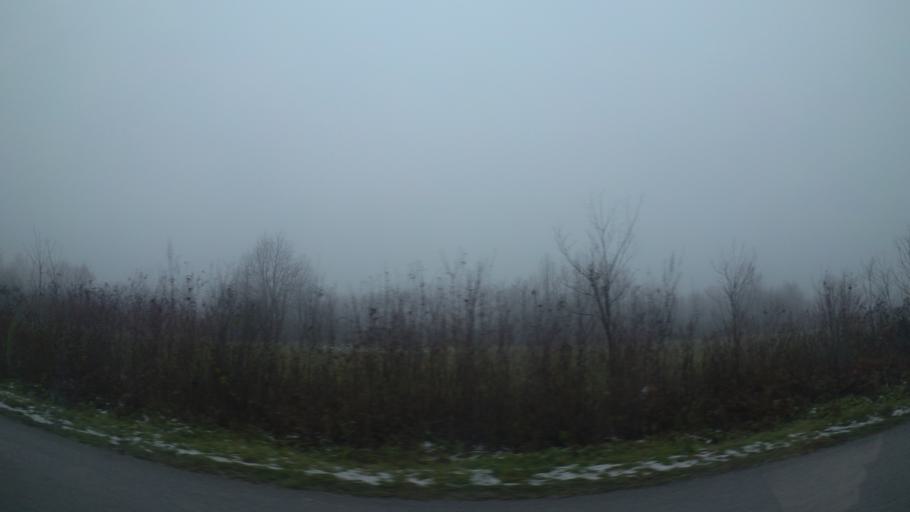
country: HR
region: Sisacko-Moslavacka
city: Glina
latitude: 45.3264
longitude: 16.0385
